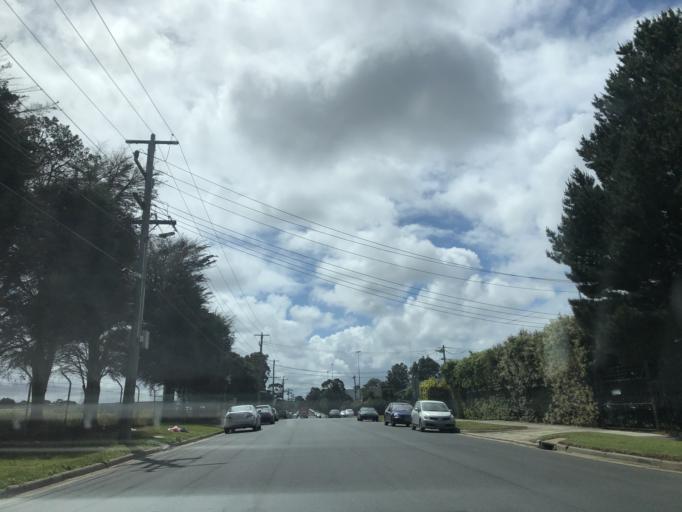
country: AU
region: Victoria
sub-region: Monash
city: Oakleigh South
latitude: -37.9315
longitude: 145.0940
